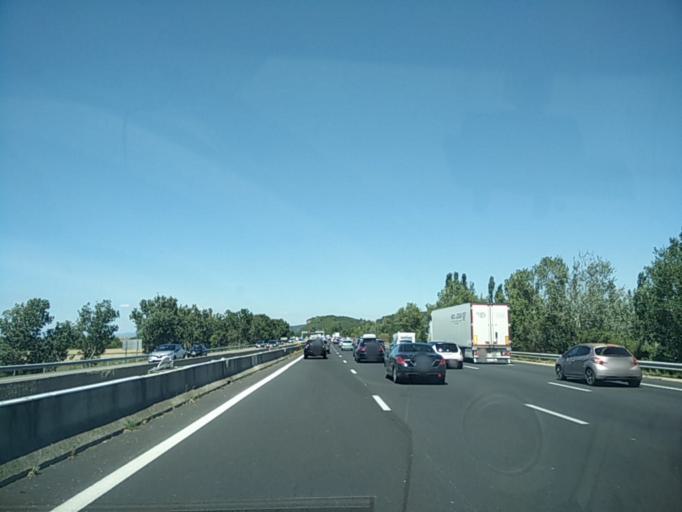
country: FR
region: Provence-Alpes-Cote d'Azur
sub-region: Departement du Vaucluse
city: Piolenc
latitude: 44.1548
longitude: 4.7716
